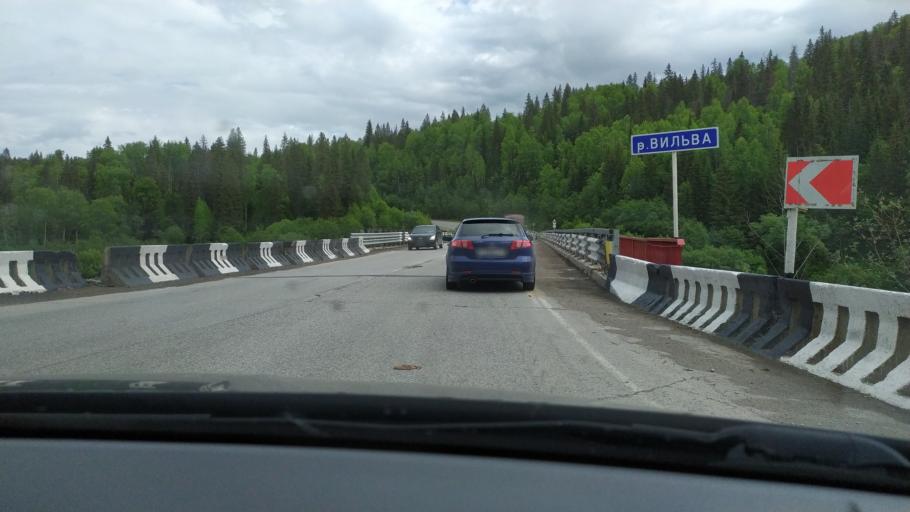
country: RU
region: Perm
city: Gremyachinsk
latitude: 58.4419
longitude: 57.8751
